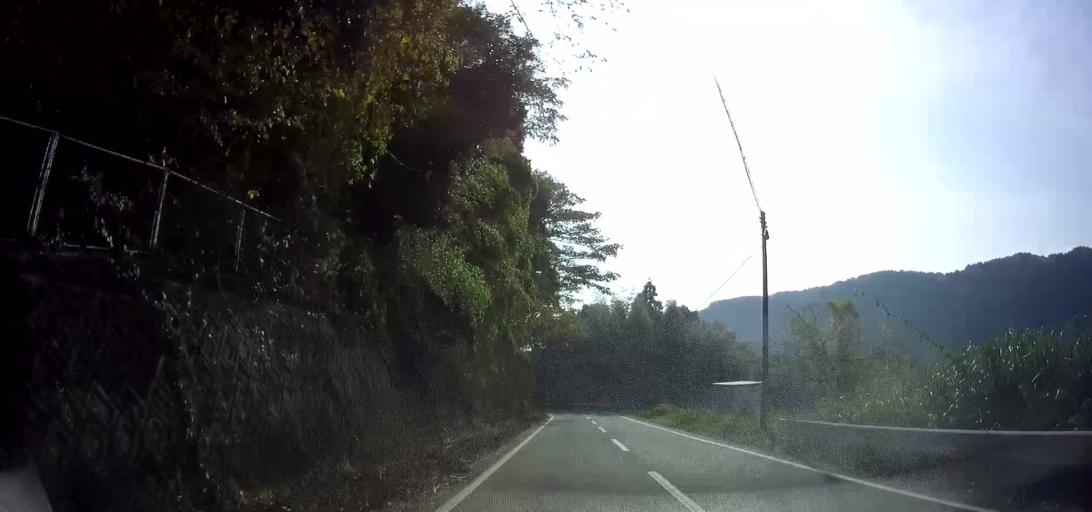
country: JP
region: Nagasaki
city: Shimabara
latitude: 32.6763
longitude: 130.2069
